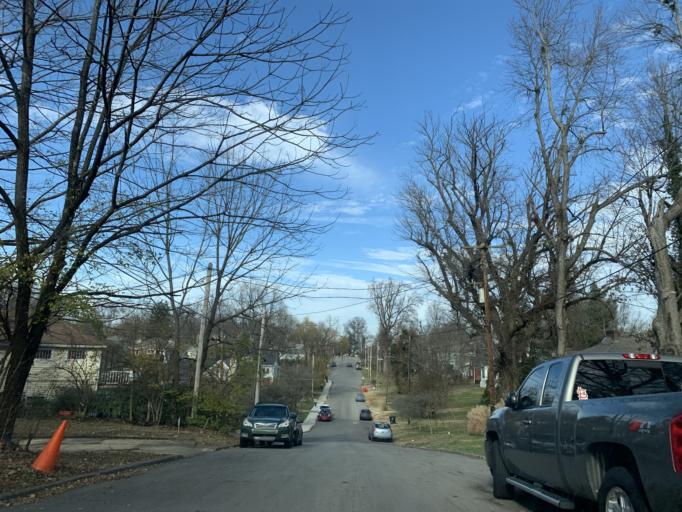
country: US
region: Kentucky
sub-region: Jefferson County
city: Indian Hills
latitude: 38.2510
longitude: -85.6993
